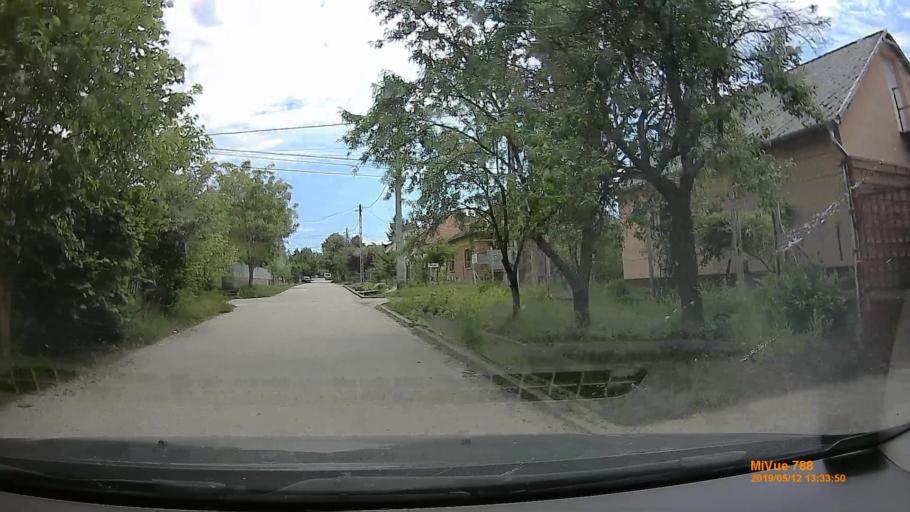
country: HU
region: Pest
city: Ecser
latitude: 47.4767
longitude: 19.2995
